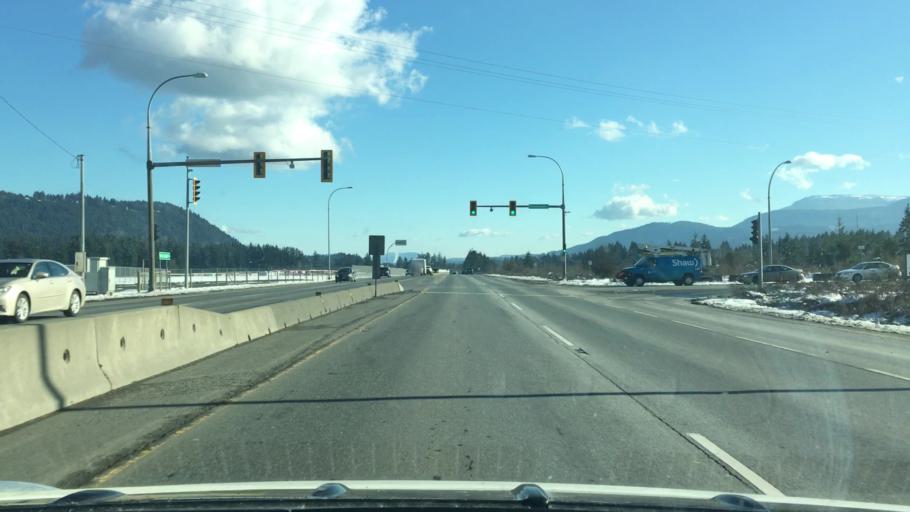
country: CA
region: British Columbia
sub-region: Cowichan Valley Regional District
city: Ladysmith
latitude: 49.0461
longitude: -123.8742
